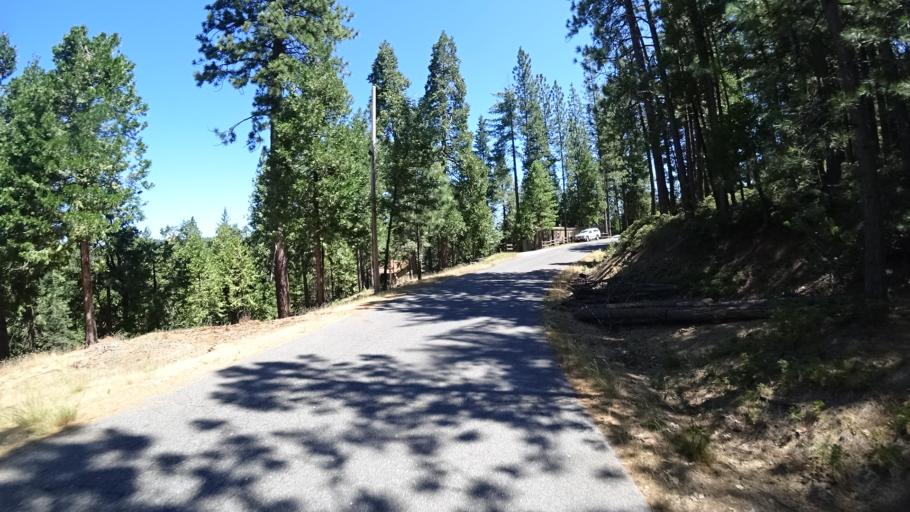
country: US
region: California
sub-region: Calaveras County
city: Arnold
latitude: 38.2301
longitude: -120.3430
